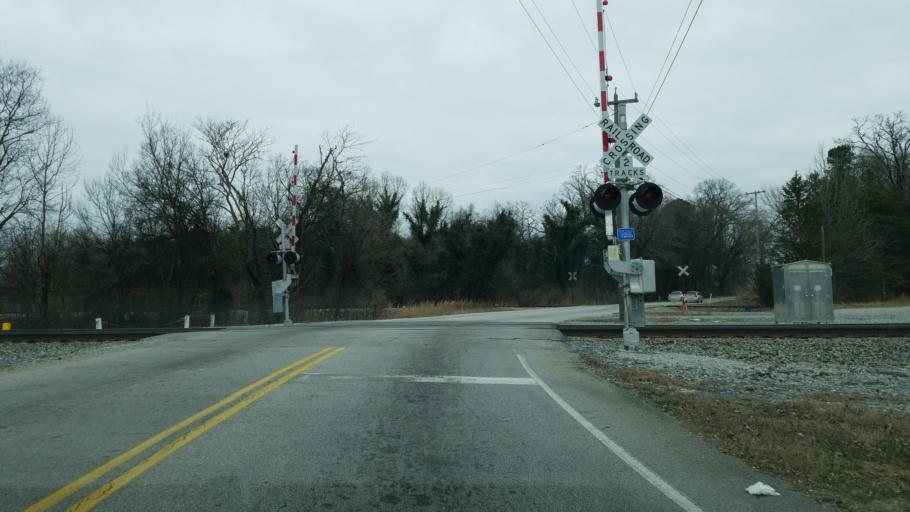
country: US
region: Tennessee
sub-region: Hamilton County
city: Harrison
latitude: 35.0667
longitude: -85.1573
